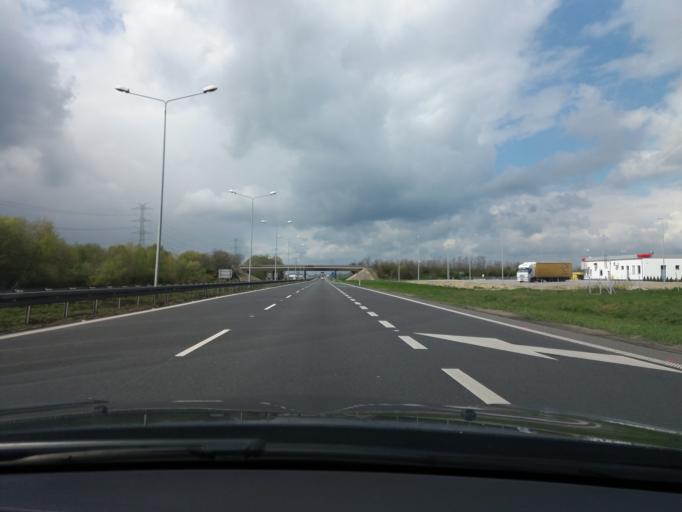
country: PL
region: Opole Voivodeship
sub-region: Powiat brzeski
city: Grodkow
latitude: 50.7826
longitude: 17.3479
